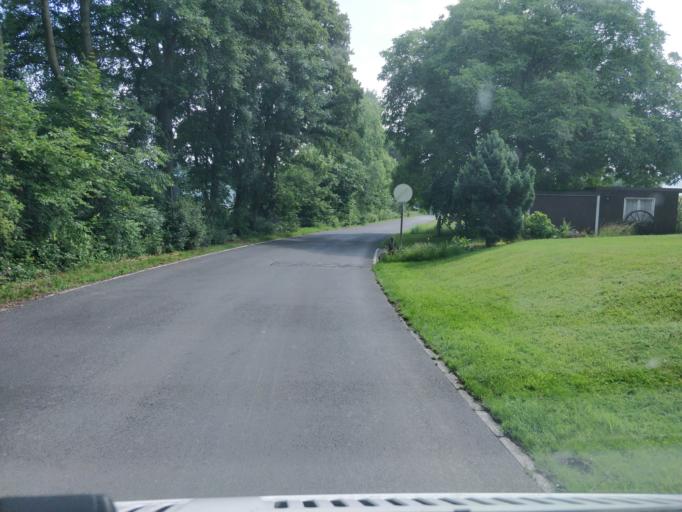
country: DE
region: North Rhine-Westphalia
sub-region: Regierungsbezirk Koln
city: Numbrecht
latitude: 50.9100
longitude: 7.5716
